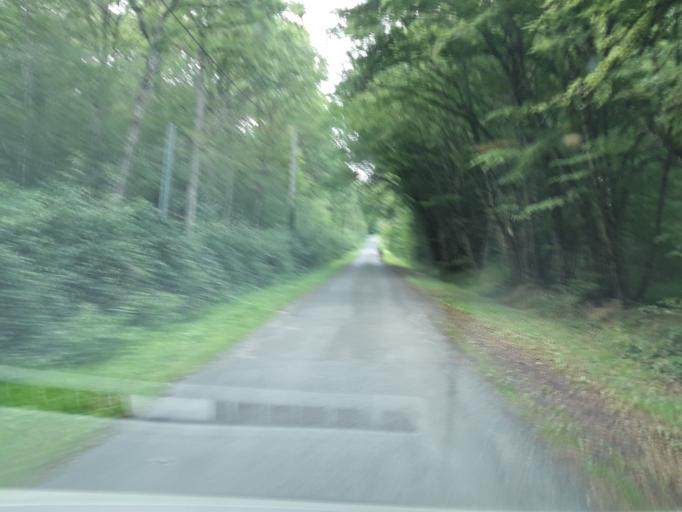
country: FR
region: Centre
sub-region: Departement du Loiret
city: Chilleurs-aux-Bois
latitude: 48.0539
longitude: 2.1585
